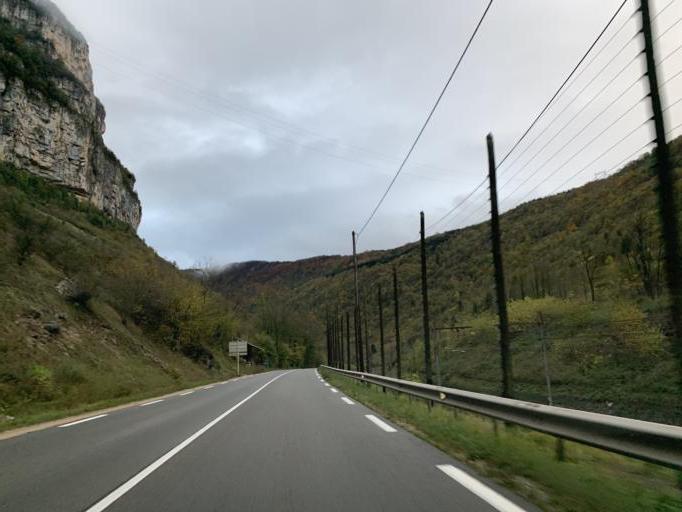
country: FR
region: Rhone-Alpes
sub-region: Departement de l'Ain
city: Tenay
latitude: 45.9080
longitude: 5.5122
